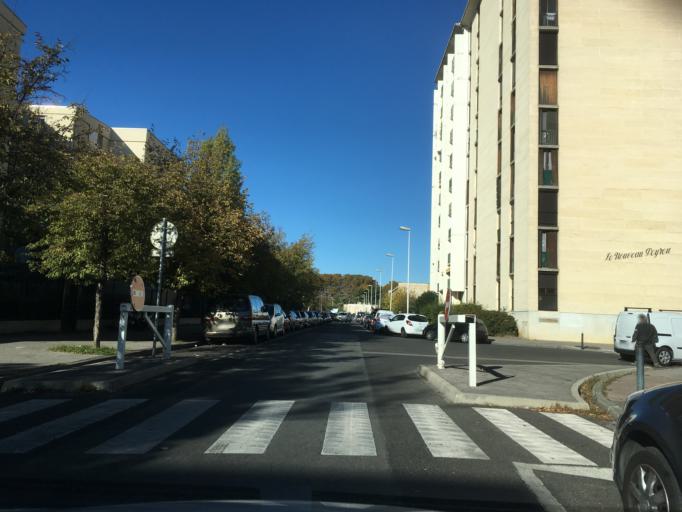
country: FR
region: Languedoc-Roussillon
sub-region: Departement de l'Herault
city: Juvignac
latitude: 43.6236
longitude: 3.8134
